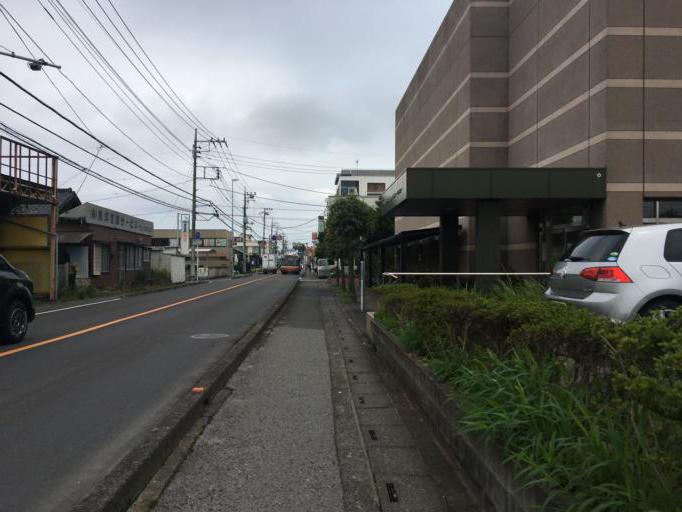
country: JP
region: Saitama
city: Ageoshimo
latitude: 35.9584
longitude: 139.6006
